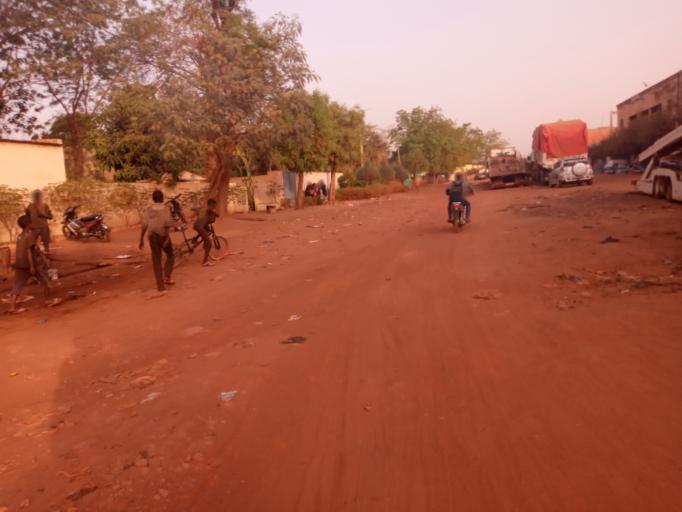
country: ML
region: Bamako
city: Bamako
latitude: 12.5937
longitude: -7.9599
